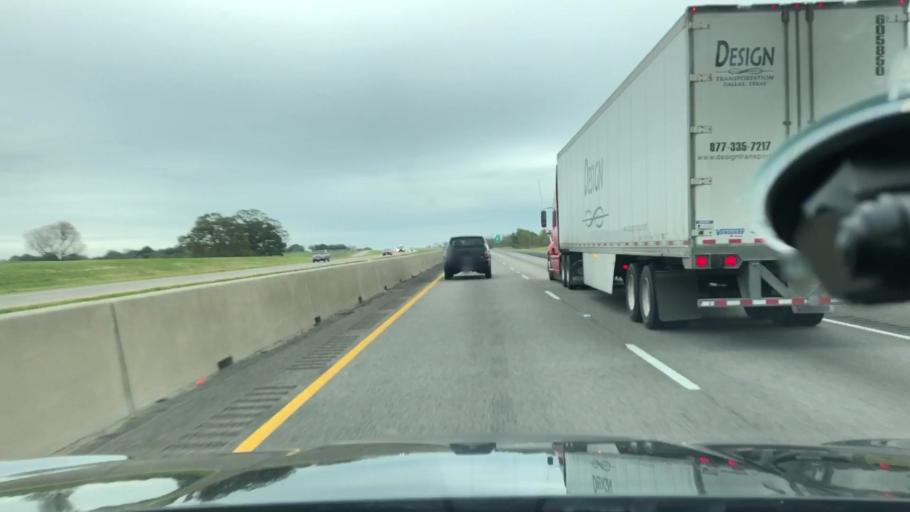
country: US
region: Texas
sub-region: Hopkins County
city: Sulphur Springs
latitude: 33.1470
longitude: -95.5197
